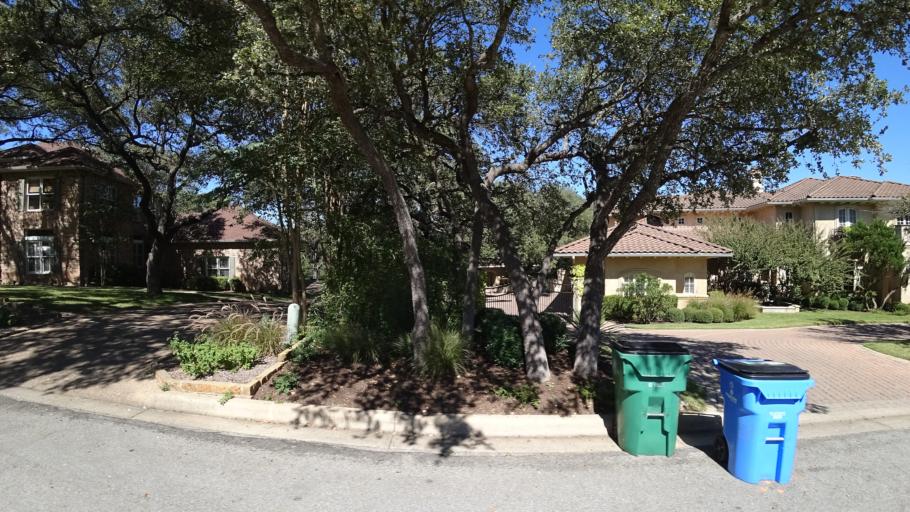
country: US
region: Texas
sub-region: Travis County
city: West Lake Hills
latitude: 30.3214
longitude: -97.7837
